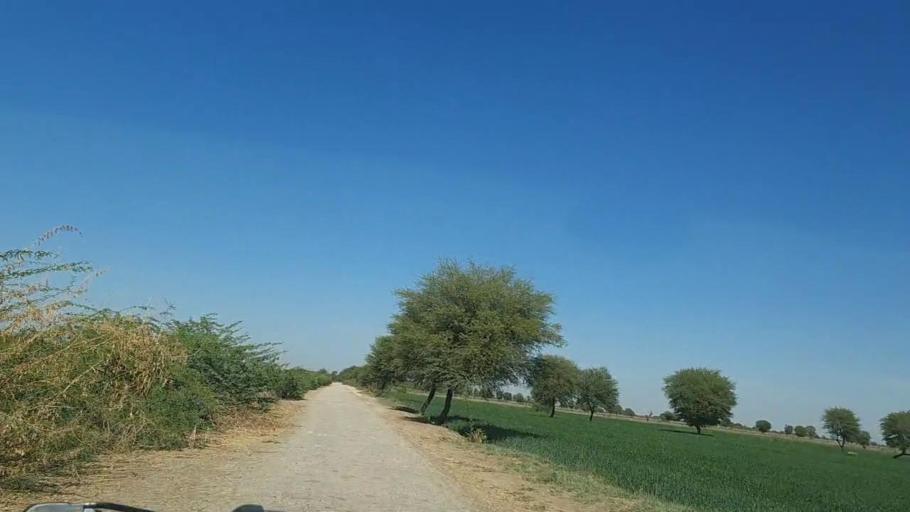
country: PK
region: Sindh
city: Dhoro Naro
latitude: 25.5221
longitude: 69.5061
